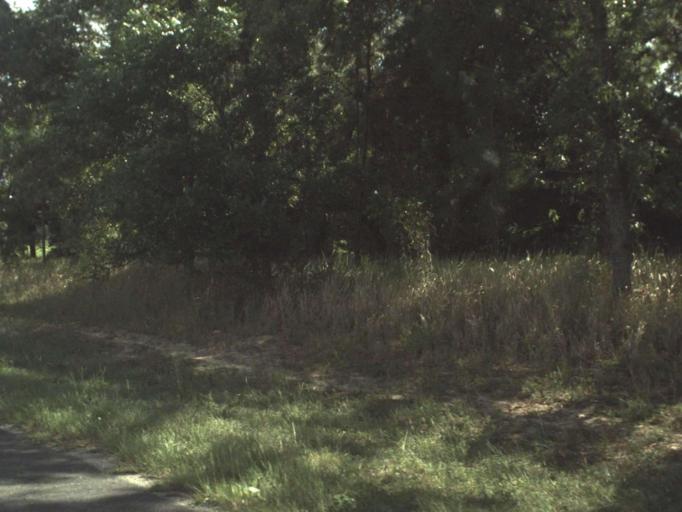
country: US
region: Florida
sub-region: Marion County
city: Silver Springs Shores
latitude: 29.1324
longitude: -82.0537
